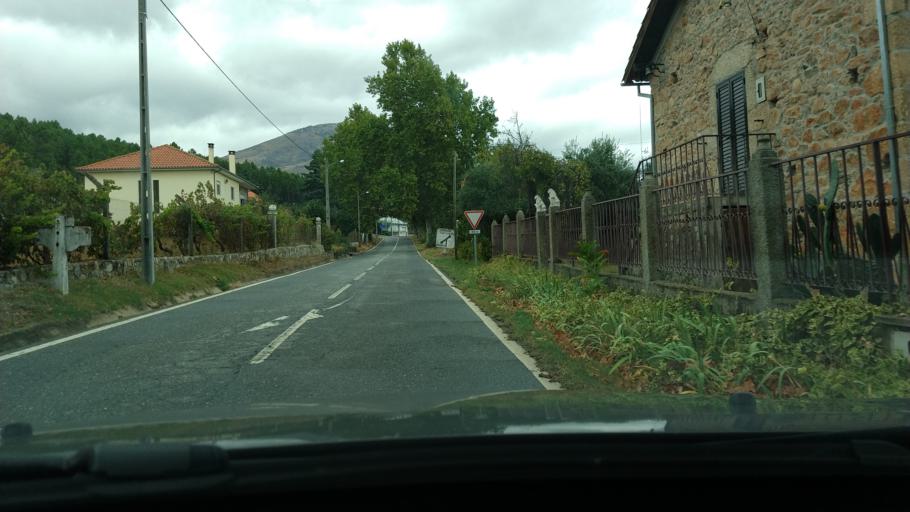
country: PT
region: Castelo Branco
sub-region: Covilha
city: Covilha
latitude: 40.2390
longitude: -7.5948
